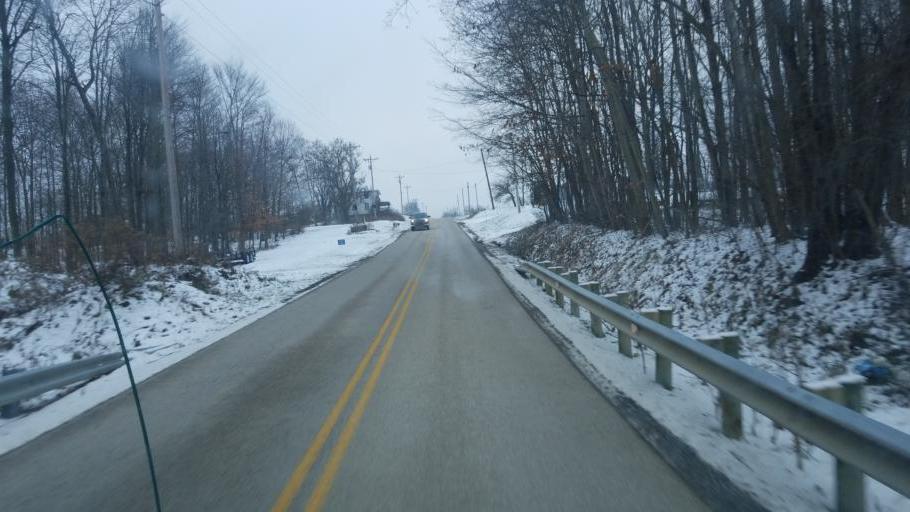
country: US
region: Ohio
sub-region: Richland County
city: Lincoln Heights
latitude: 40.6911
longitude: -82.4169
